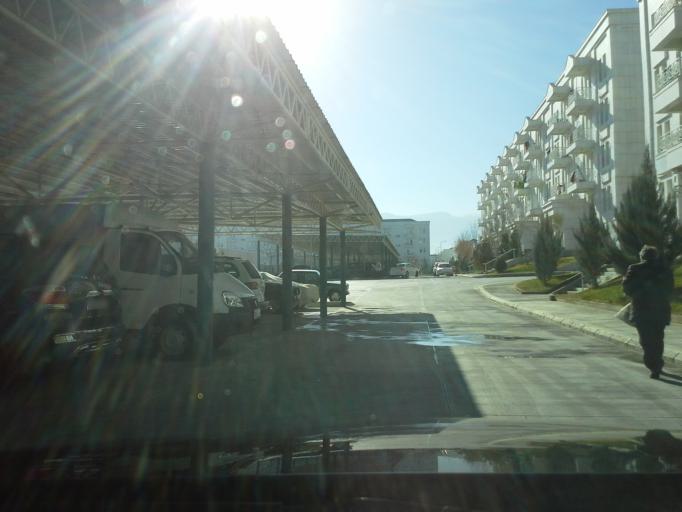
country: TM
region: Ahal
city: Ashgabat
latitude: 37.9729
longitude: 58.3385
